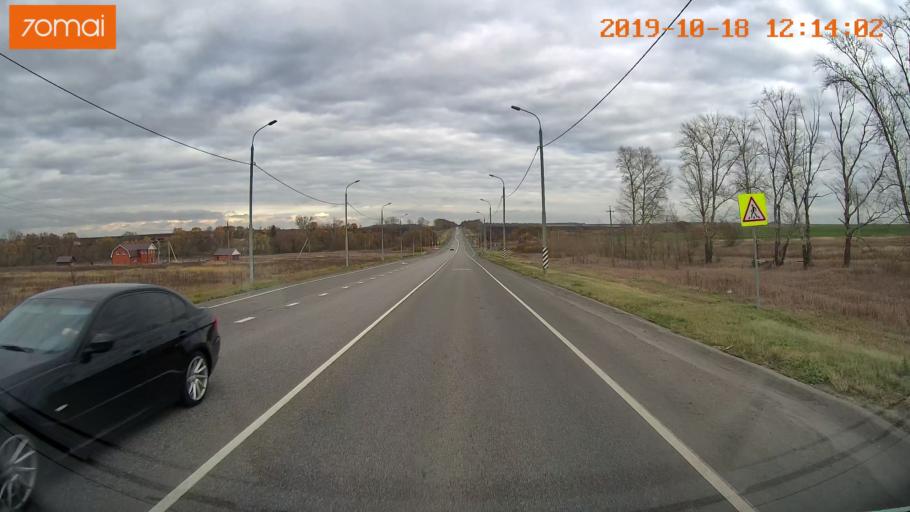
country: RU
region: Rjazan
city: Zakharovo
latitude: 54.4257
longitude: 39.3766
